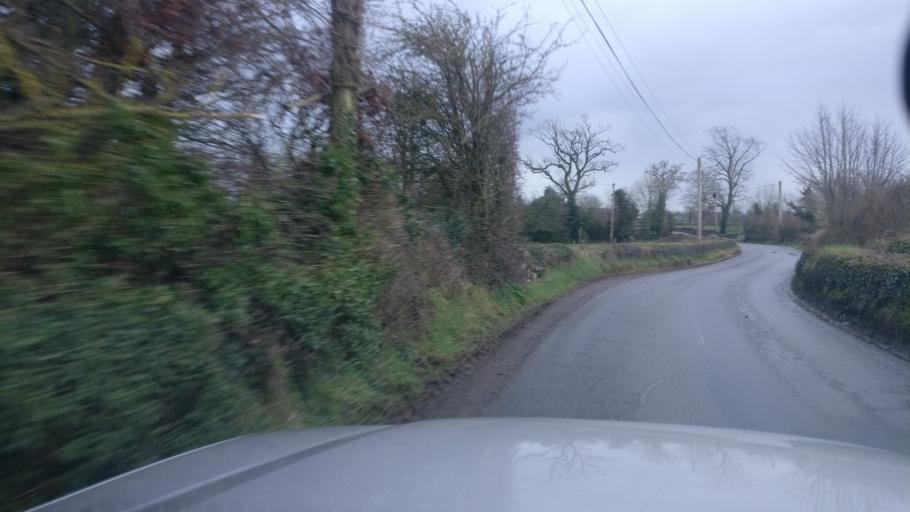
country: IE
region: Munster
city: Nenagh Bridge
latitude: 52.9853
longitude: -8.1084
